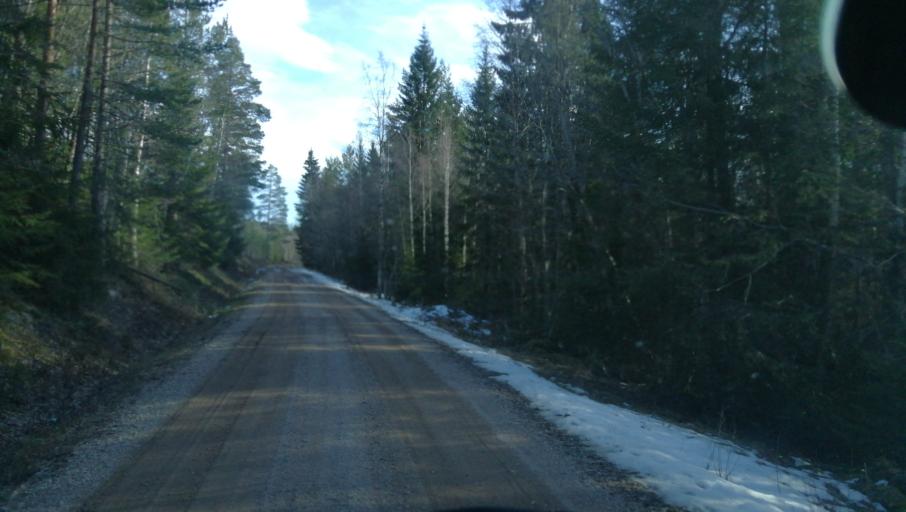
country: SE
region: Dalarna
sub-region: Vansbro Kommun
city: Vansbro
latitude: 60.8201
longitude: 14.1961
